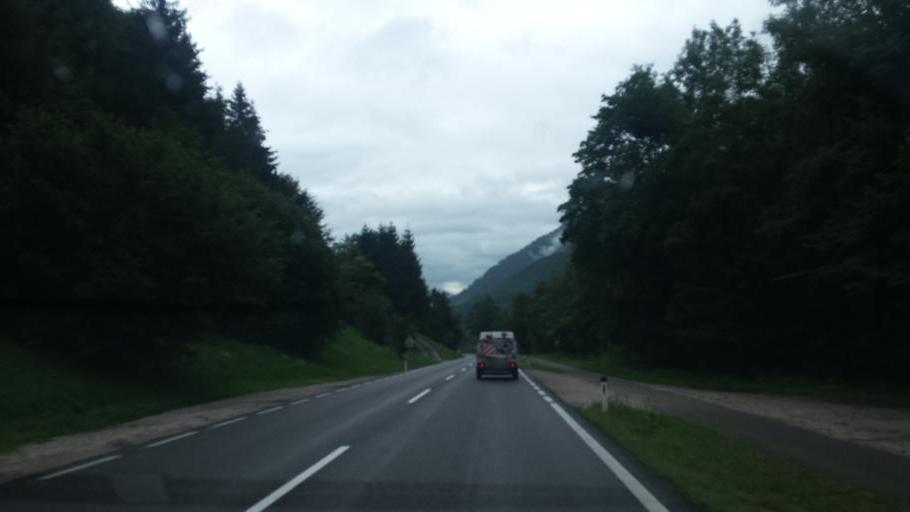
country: AT
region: Upper Austria
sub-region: Politischer Bezirk Gmunden
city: Bad Ischl
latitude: 47.7513
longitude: 13.6928
